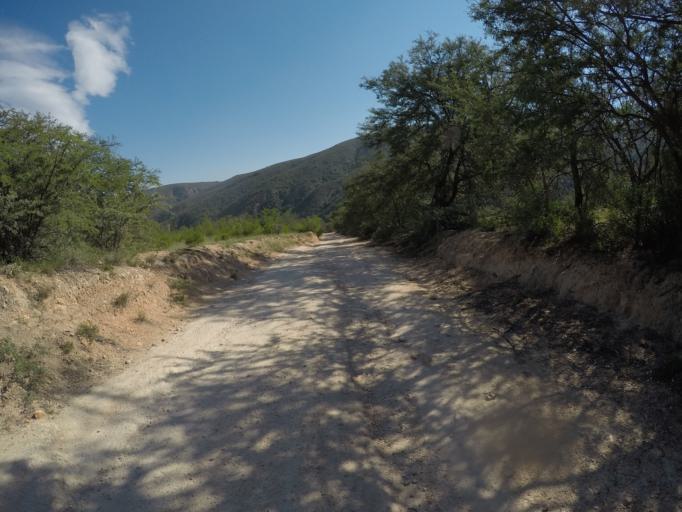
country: ZA
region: Eastern Cape
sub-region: Cacadu District Municipality
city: Kareedouw
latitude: -33.6459
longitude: 24.4610
